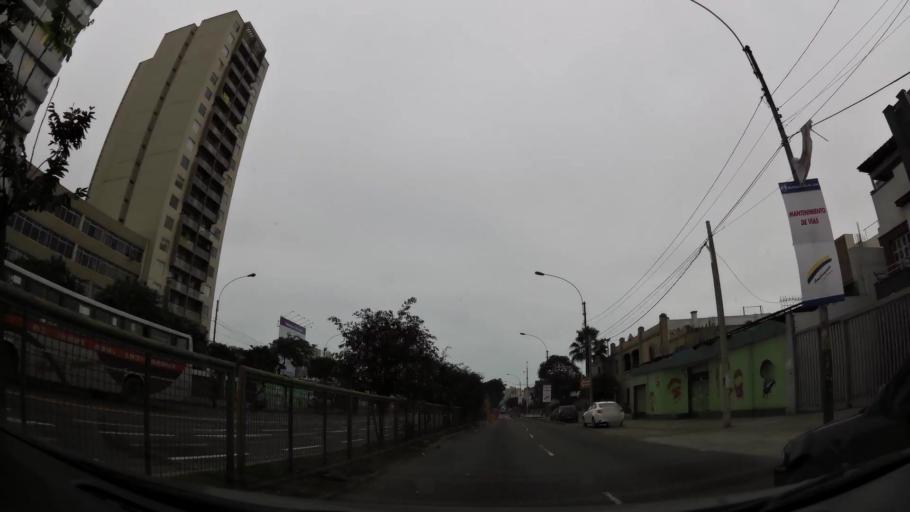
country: PE
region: Lima
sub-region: Lima
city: San Isidro
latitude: -12.0798
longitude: -77.0579
